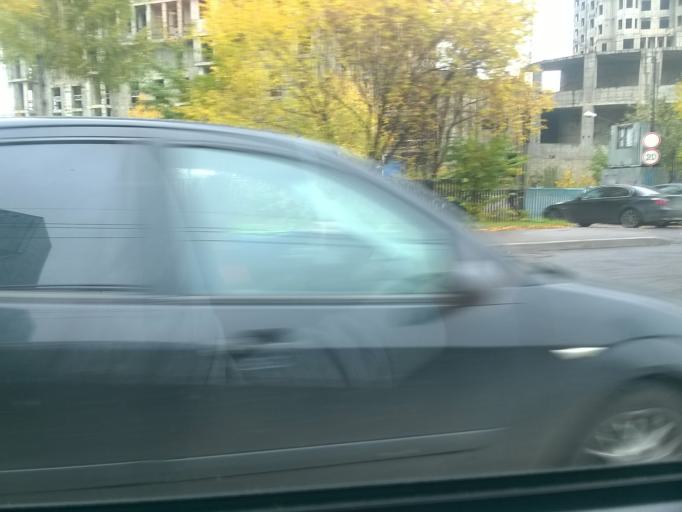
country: RU
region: Moscow
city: Troparevo
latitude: 55.6671
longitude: 37.4806
